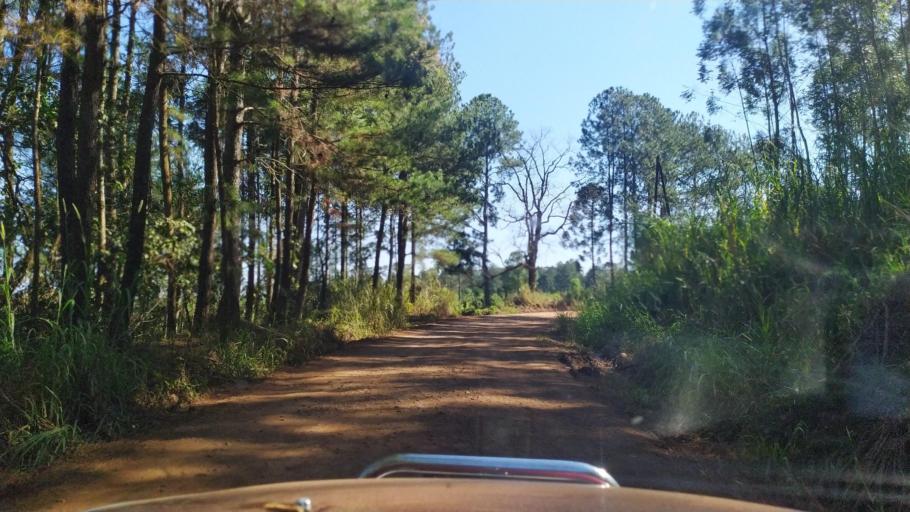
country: AR
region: Misiones
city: El Alcazar
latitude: -26.7235
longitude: -54.6852
